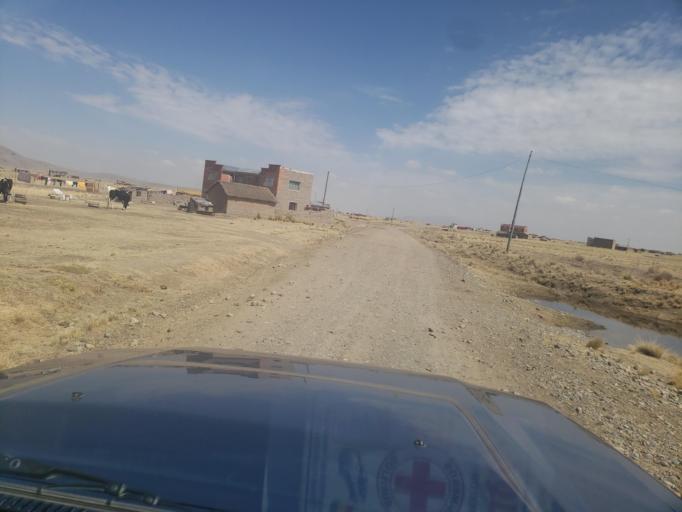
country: BO
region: La Paz
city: Batallas
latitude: -16.4341
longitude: -68.3829
